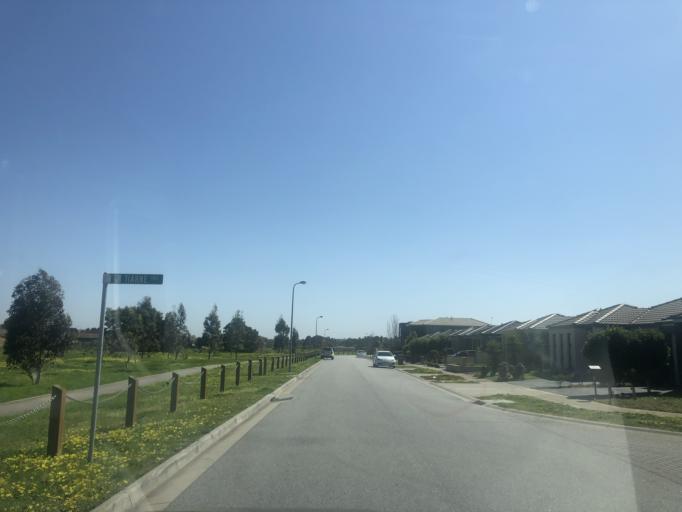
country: AU
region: Victoria
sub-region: Casey
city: Narre Warren South
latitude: -38.0514
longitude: 145.2805
